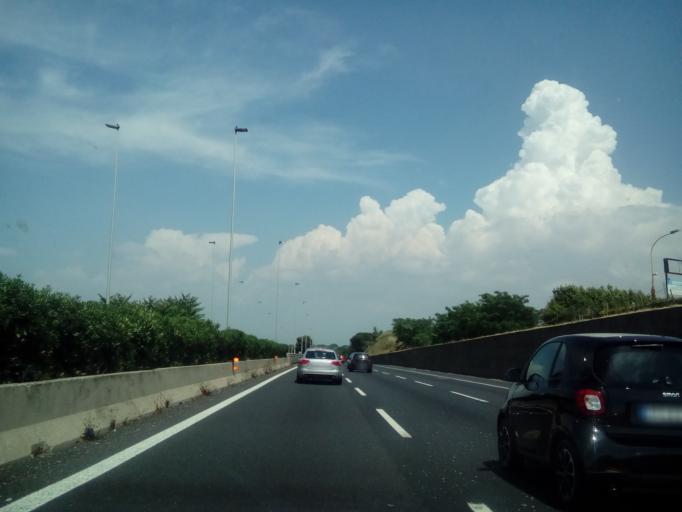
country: IT
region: Latium
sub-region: Citta metropolitana di Roma Capitale
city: Borgo Lotti
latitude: 41.7993
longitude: 12.5441
